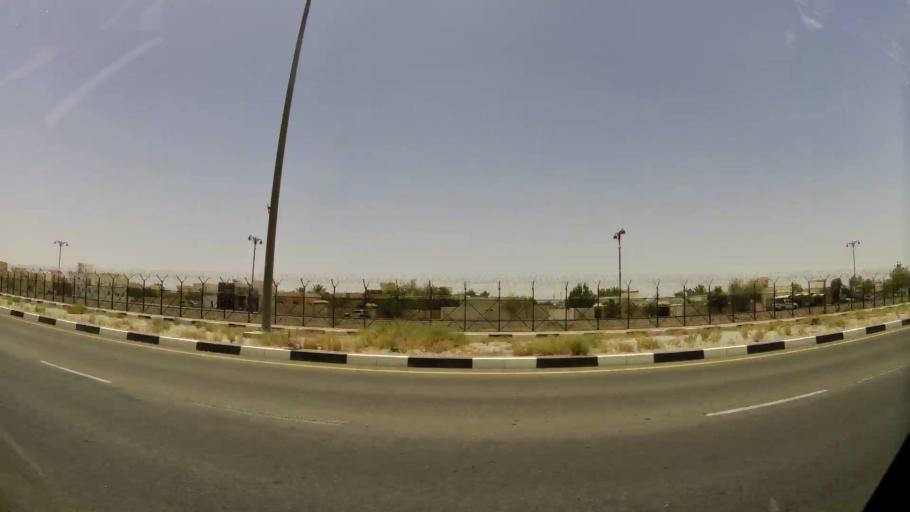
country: OM
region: Al Buraimi
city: Al Buraymi
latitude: 24.2703
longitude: 55.7790
